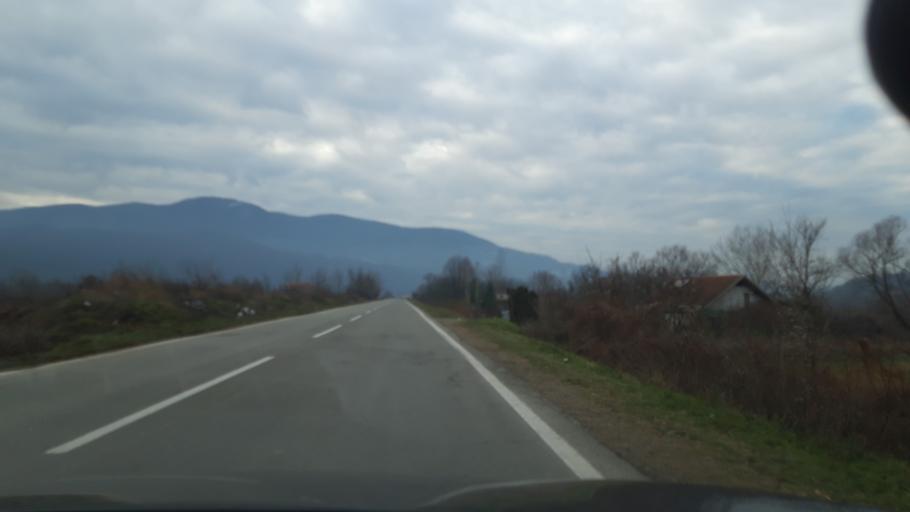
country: RS
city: Trsic
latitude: 44.5336
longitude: 19.1814
